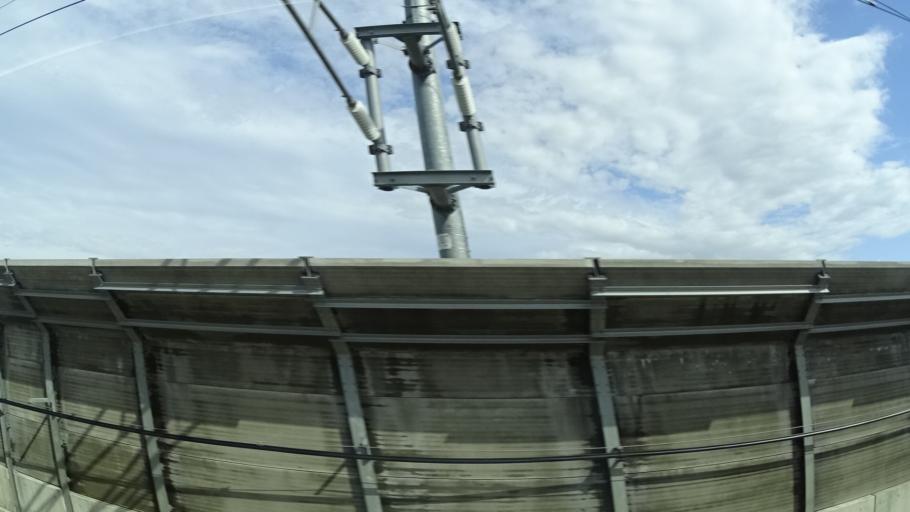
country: JP
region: Toyama
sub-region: Oyabe Shi
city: Oyabe
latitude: 36.6761
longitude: 136.9023
